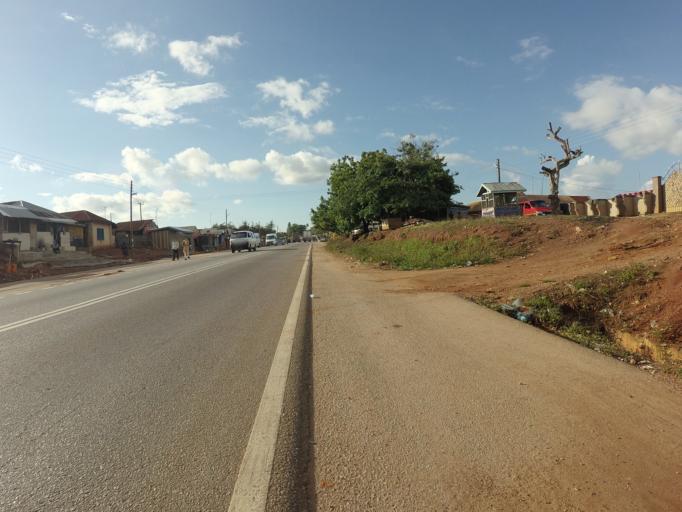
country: GH
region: Ashanti
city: Tafo
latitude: 6.9056
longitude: -1.6555
